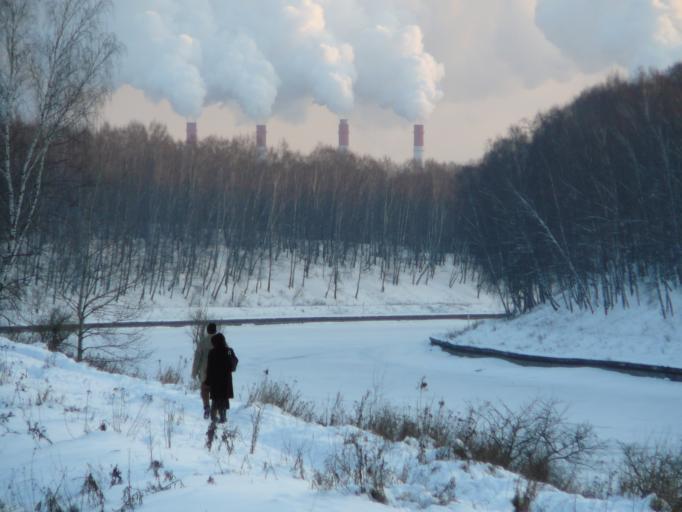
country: RU
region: Moskovskaya
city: Dolgoprudnyy
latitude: 55.9421
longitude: 37.4821
